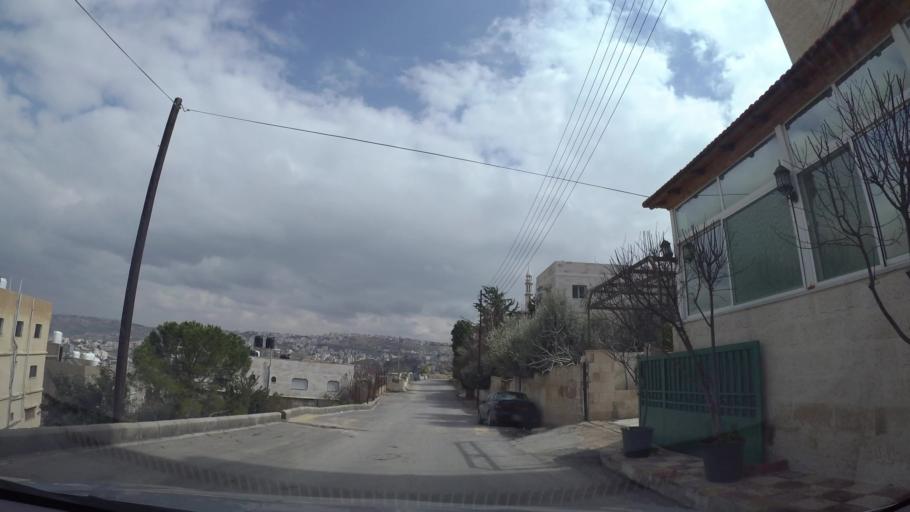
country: JO
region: Amman
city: Al Jubayhah
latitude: 32.0363
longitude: 35.8233
